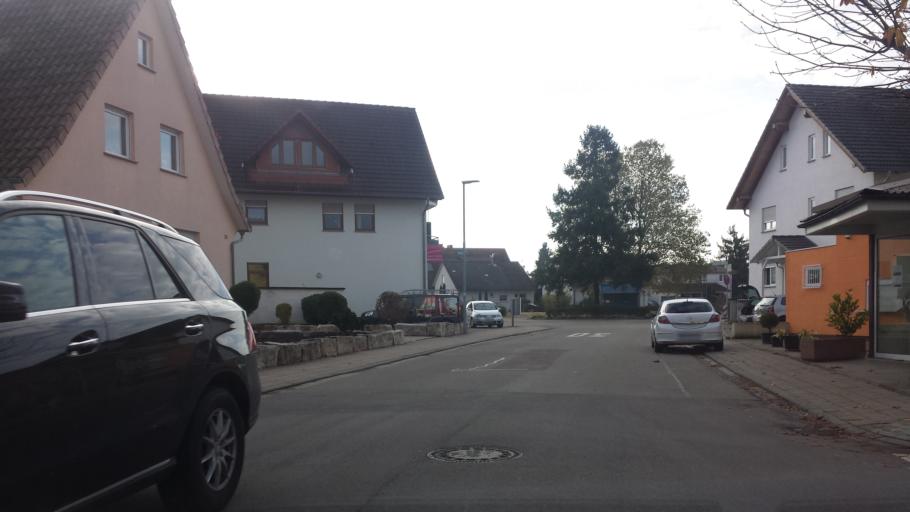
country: DE
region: Baden-Wuerttemberg
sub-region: Karlsruhe Region
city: Sankt Leon-Rot
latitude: 49.2605
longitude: 8.6336
